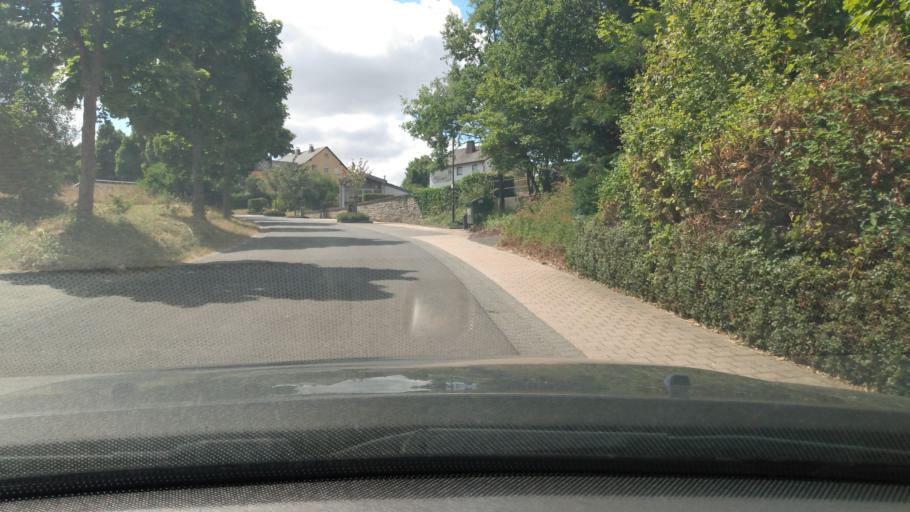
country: DE
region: Rheinland-Pfalz
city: Kommen
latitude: 49.8636
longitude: 7.1630
